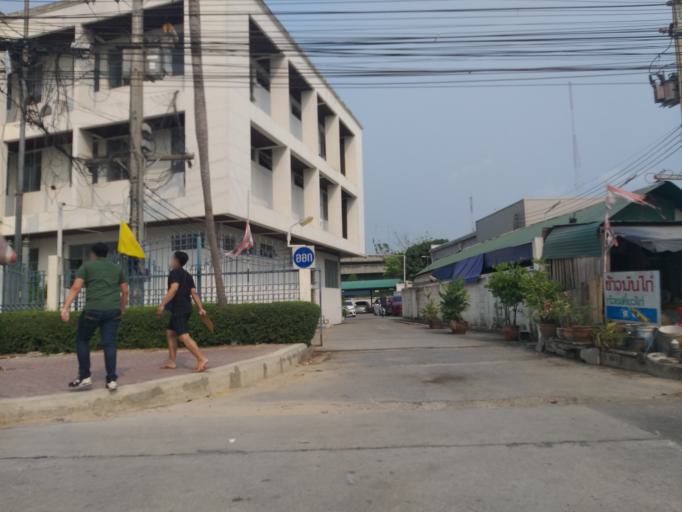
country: TH
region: Phra Nakhon Si Ayutthaya
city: Ban Bang Kadi Pathum Thani
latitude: 14.0016
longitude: 100.5705
